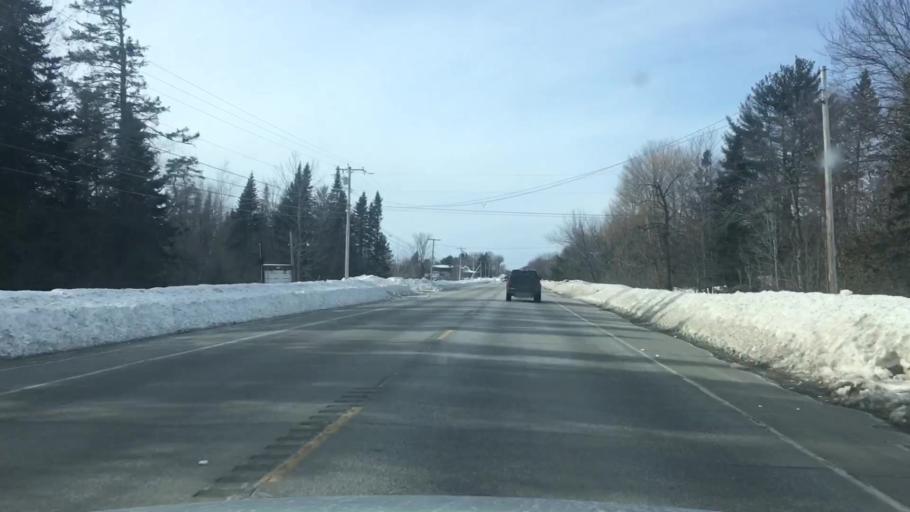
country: US
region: Maine
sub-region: Penobscot County
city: Kenduskeag
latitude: 44.9786
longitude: -68.9923
